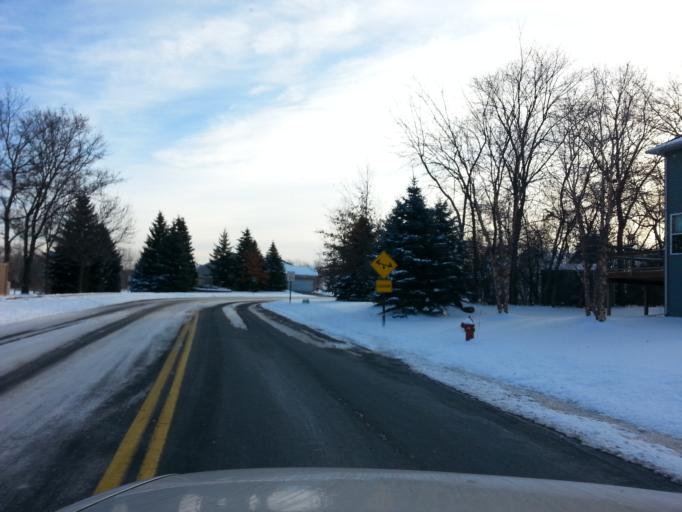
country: US
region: Minnesota
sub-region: Scott County
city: Savage
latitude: 44.7676
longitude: -93.3948
